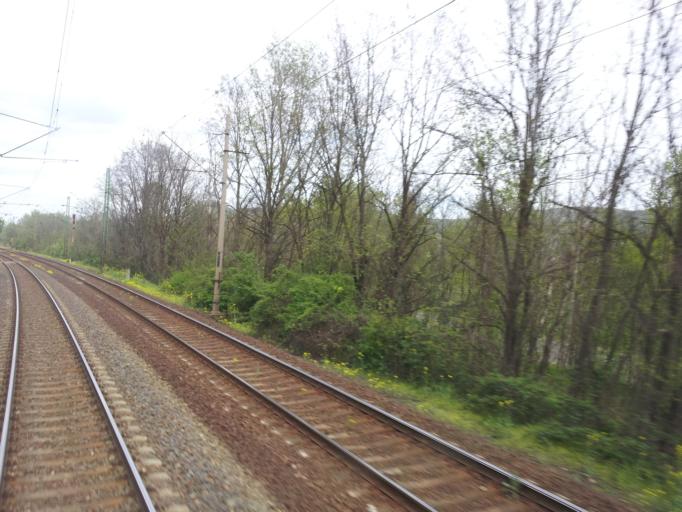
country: HU
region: Pest
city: Nagymaros
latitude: 47.7754
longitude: 18.9481
